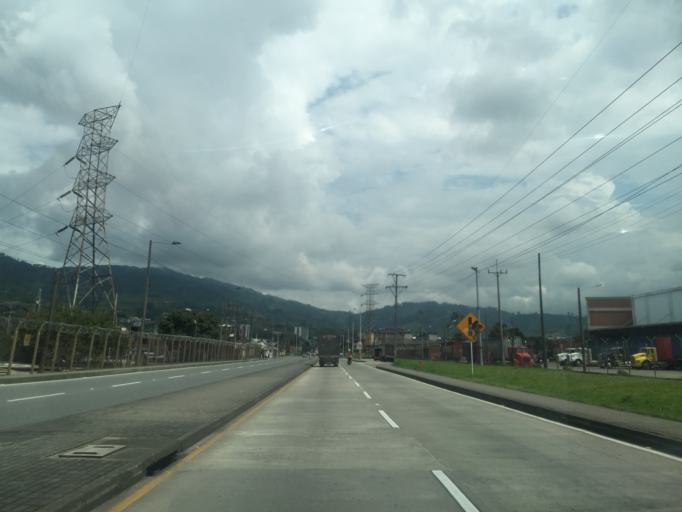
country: CO
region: Risaralda
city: Dos Quebradas
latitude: 4.8350
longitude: -75.6781
